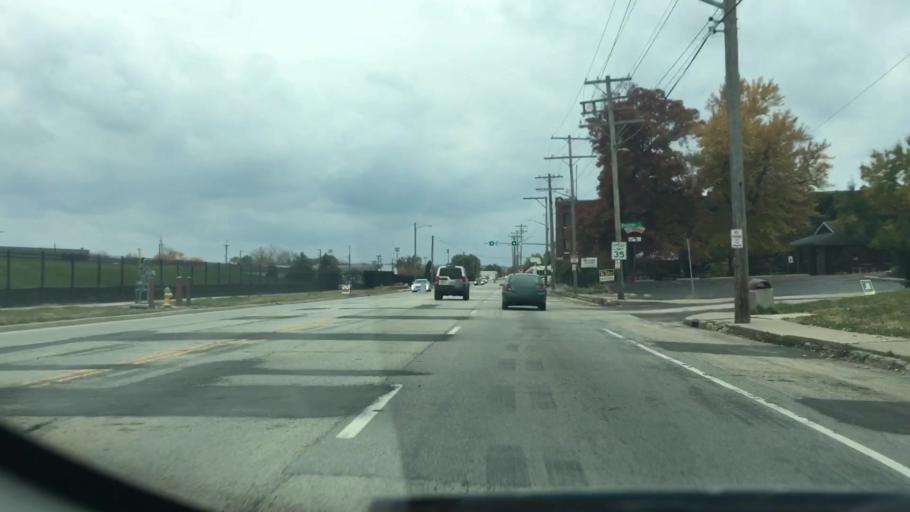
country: US
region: Illinois
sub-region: Peoria County
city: North Peoria
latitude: 40.7106
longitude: -89.5634
